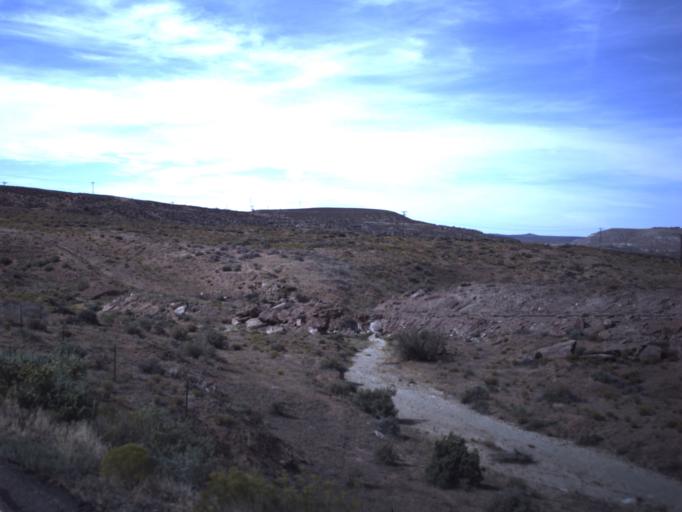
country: US
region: Utah
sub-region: San Juan County
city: Blanding
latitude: 37.2917
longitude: -109.2882
